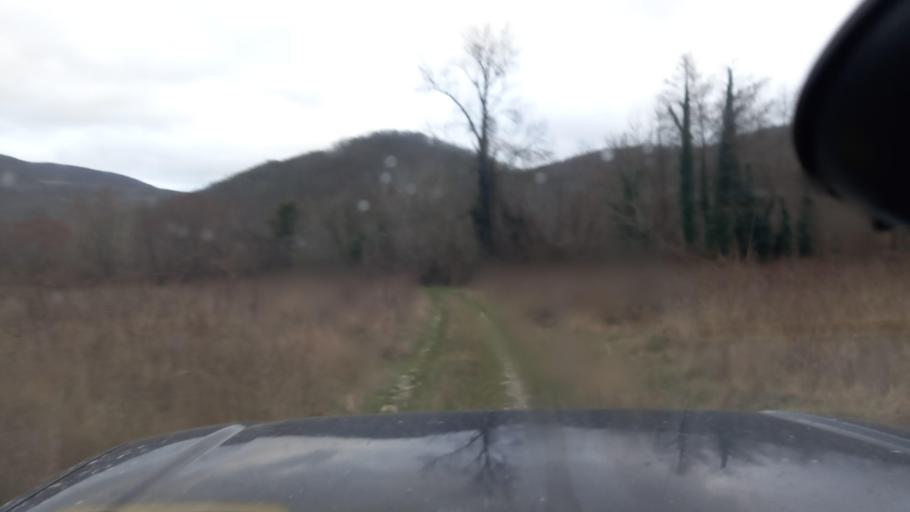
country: RU
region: Krasnodarskiy
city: Pshada
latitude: 44.4925
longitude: 38.4138
